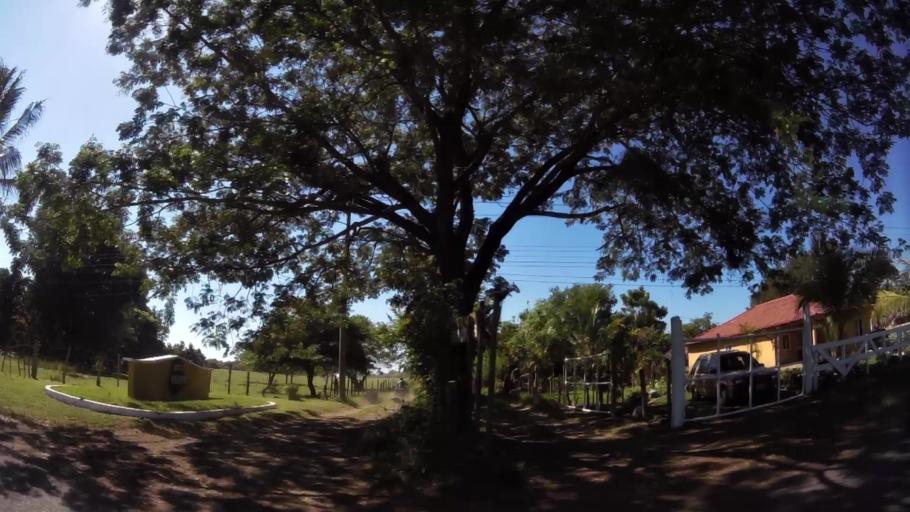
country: GT
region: Santa Rosa
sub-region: Municipio de Taxisco
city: Taxisco
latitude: 13.9098
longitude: -90.5256
